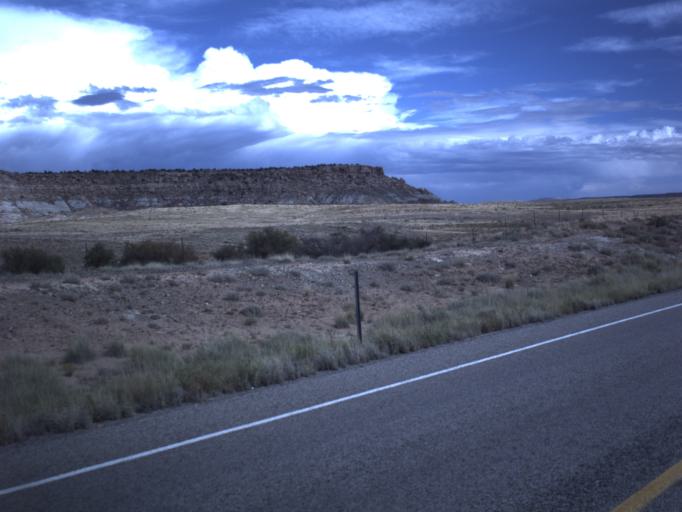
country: US
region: Colorado
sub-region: Montezuma County
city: Towaoc
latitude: 37.1642
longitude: -109.0726
